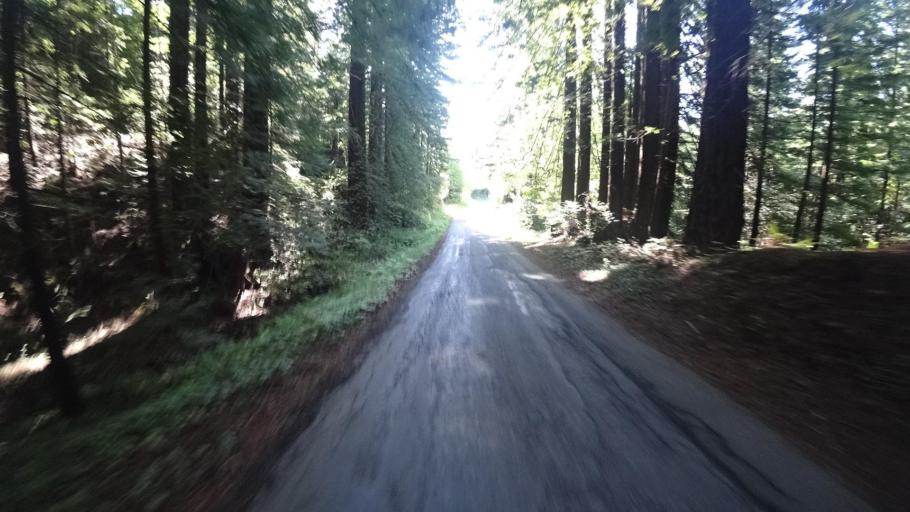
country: US
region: California
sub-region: Humboldt County
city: Rio Dell
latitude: 40.4600
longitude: -124.0420
